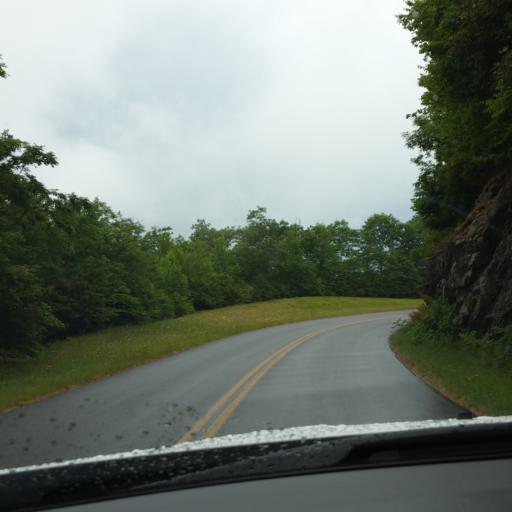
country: US
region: North Carolina
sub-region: Transylvania County
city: Brevard
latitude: 35.3831
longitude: -82.7798
